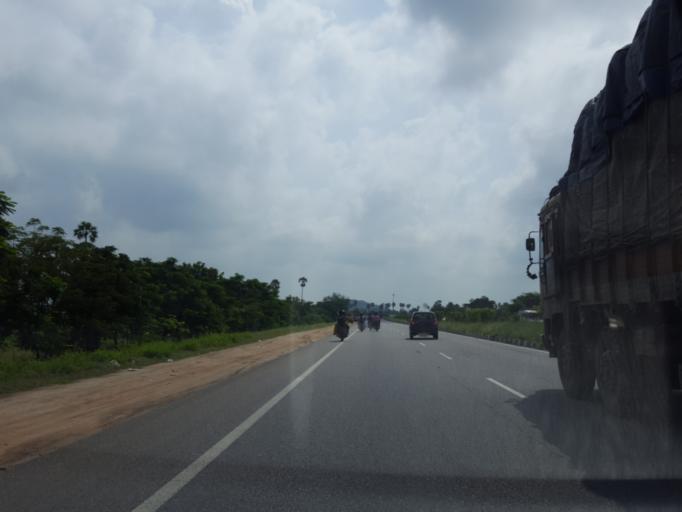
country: IN
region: Telangana
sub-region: Nalgonda
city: Bhongir
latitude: 17.2301
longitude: 78.9697
